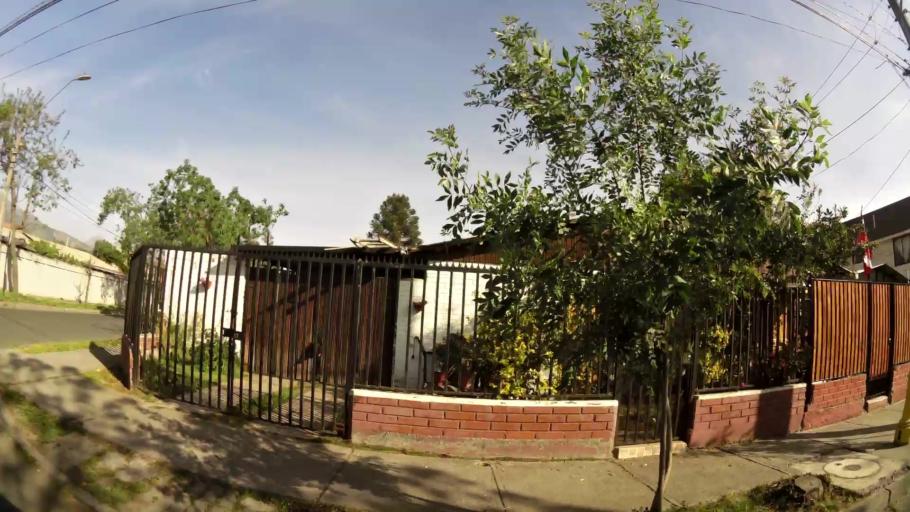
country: CL
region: Santiago Metropolitan
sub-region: Provincia de Santiago
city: Villa Presidente Frei, Nunoa, Santiago, Chile
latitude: -33.5342
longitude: -70.5766
